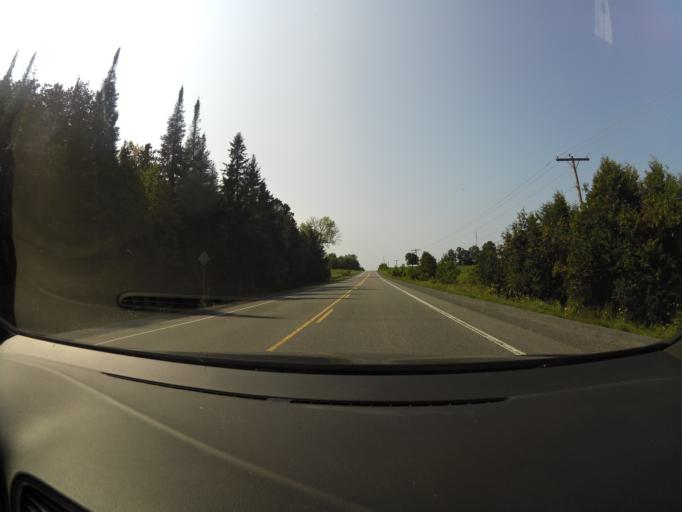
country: CA
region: Ontario
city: Arnprior
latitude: 45.4735
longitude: -76.1760
